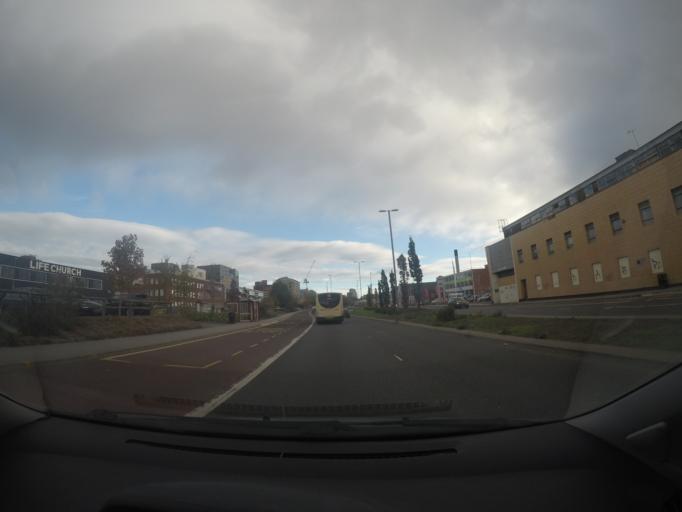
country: GB
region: England
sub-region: City and Borough of Leeds
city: Leeds
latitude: 53.8013
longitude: -1.5686
